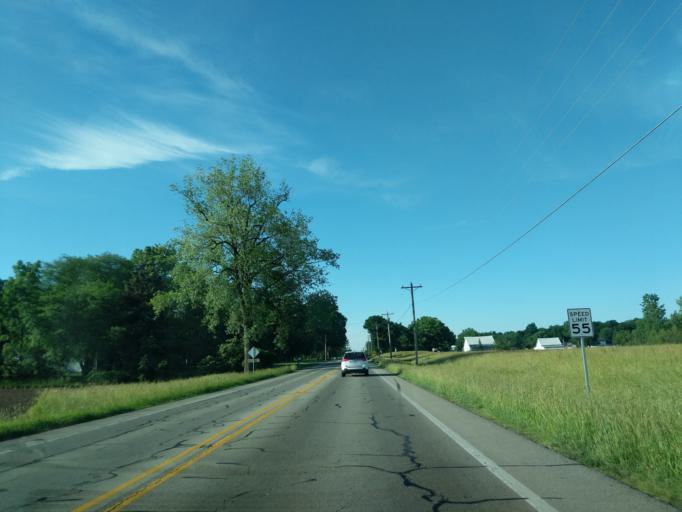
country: US
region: Indiana
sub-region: Hancock County
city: Greenfield
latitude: 39.8416
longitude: -85.7700
